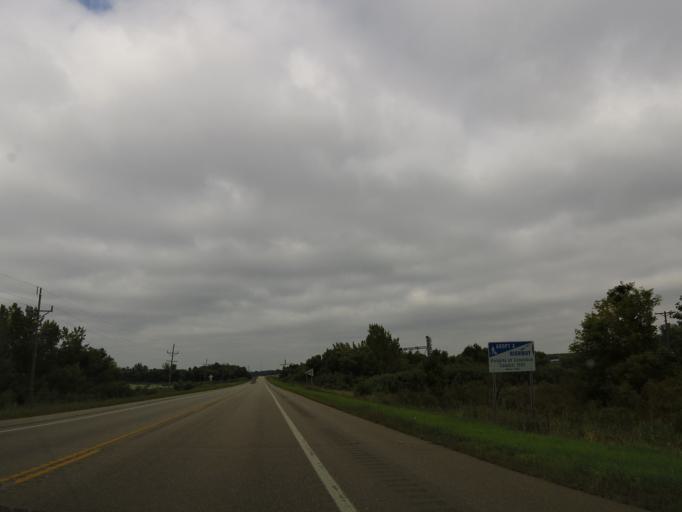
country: US
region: Minnesota
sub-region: Chippewa County
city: Montevideo
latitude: 44.9050
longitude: -95.6864
